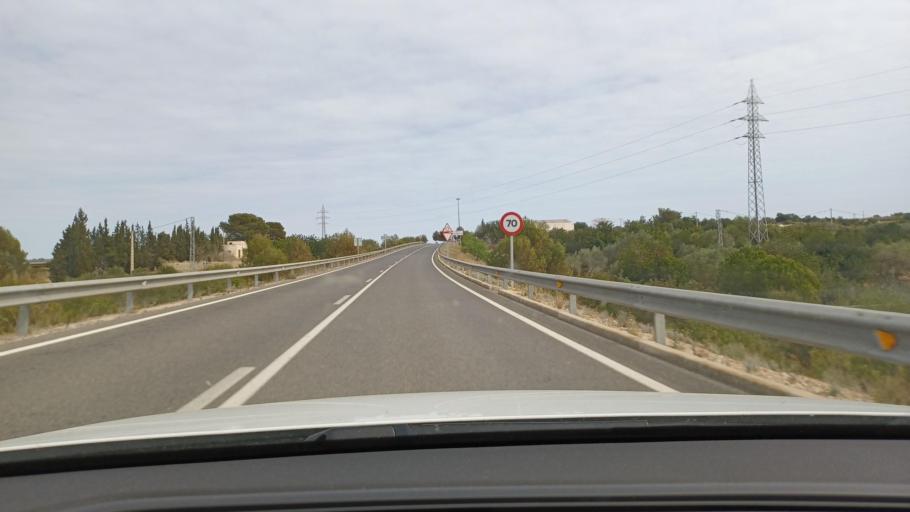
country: ES
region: Catalonia
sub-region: Provincia de Tarragona
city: Masdenverge
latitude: 40.7025
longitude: 0.5479
